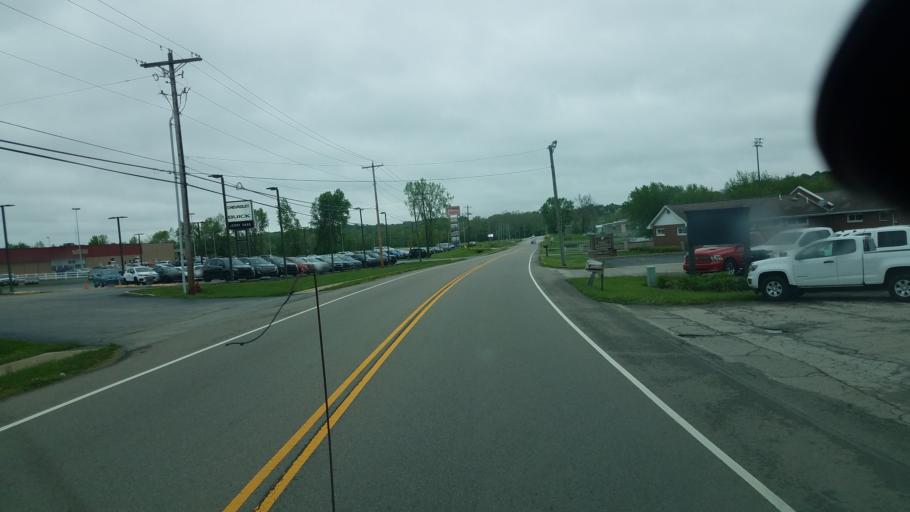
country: US
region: Ohio
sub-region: Highland County
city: Hillsboro
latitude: 39.2302
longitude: -83.6109
